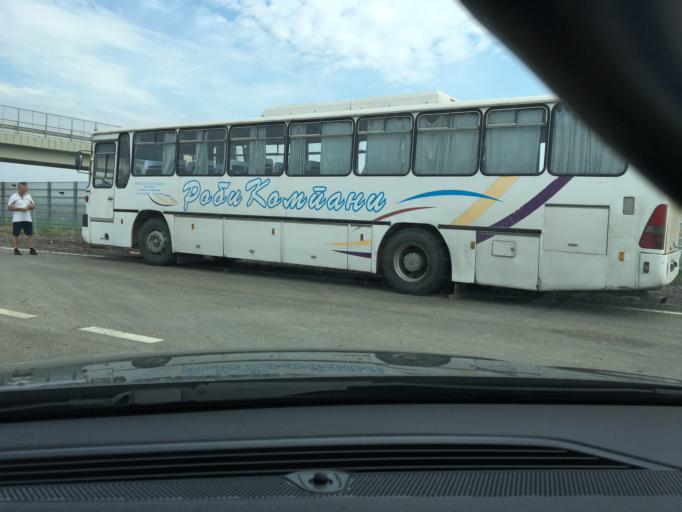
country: MK
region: Sveti Nikole
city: Sveti Nikole
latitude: 41.8103
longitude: 22.0478
